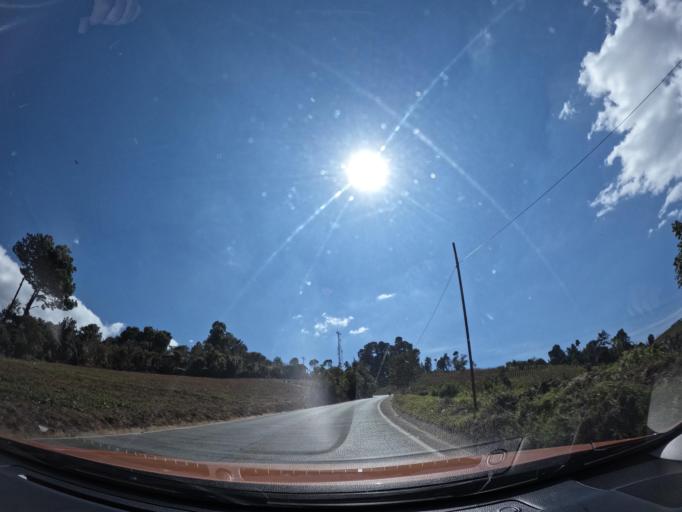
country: GT
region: Chimaltenango
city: Patzun
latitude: 14.6727
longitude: -91.0572
